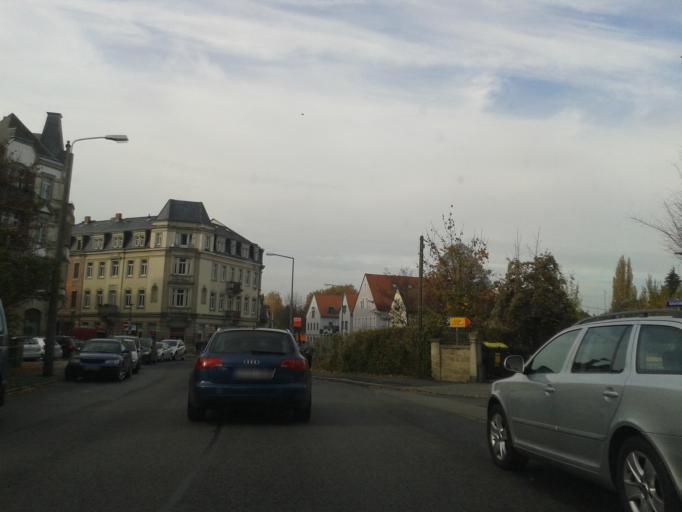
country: DE
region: Saxony
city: Dresden
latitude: 51.0274
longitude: 13.7622
